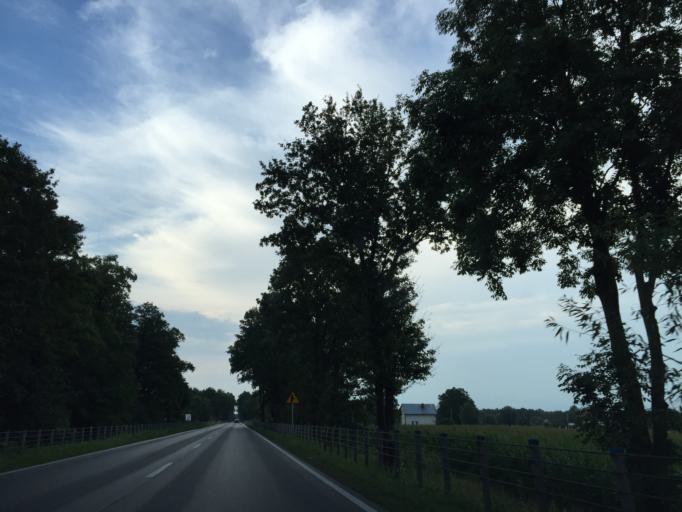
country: PL
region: Masovian Voivodeship
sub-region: Powiat wegrowski
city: Sadowne
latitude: 52.6691
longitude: 21.8494
